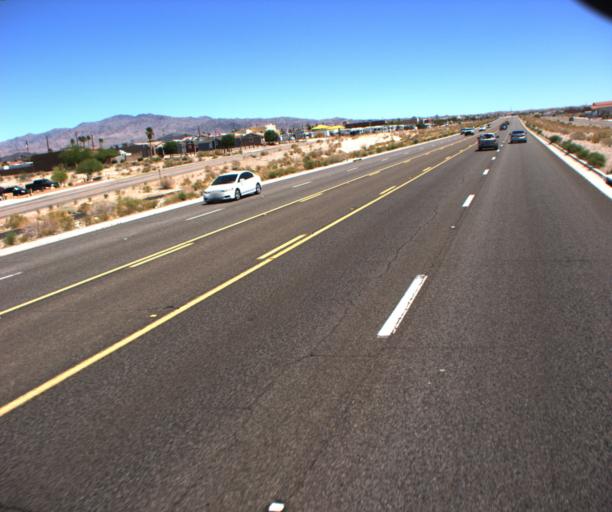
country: US
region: Arizona
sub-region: Mohave County
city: Lake Havasu City
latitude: 34.4553
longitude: -114.2932
